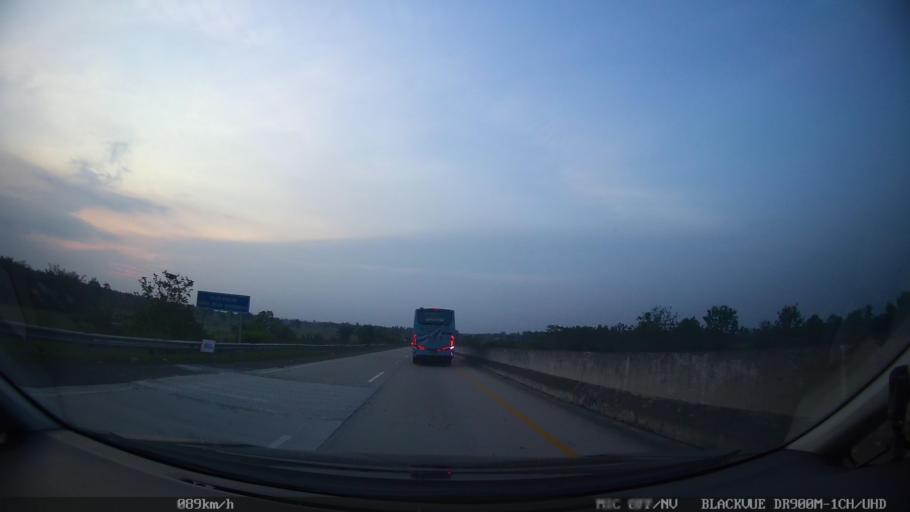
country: ID
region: Lampung
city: Kalianda
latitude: -5.6820
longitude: 105.6111
